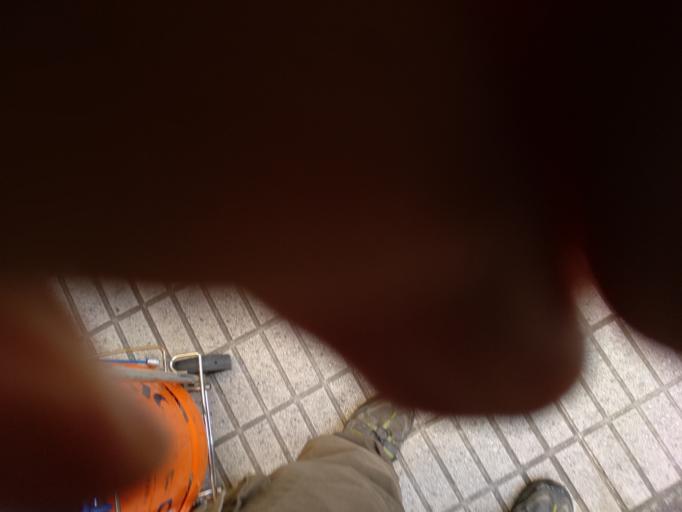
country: ES
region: Asturias
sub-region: Province of Asturias
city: Gijon
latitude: 43.5368
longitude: -5.6678
